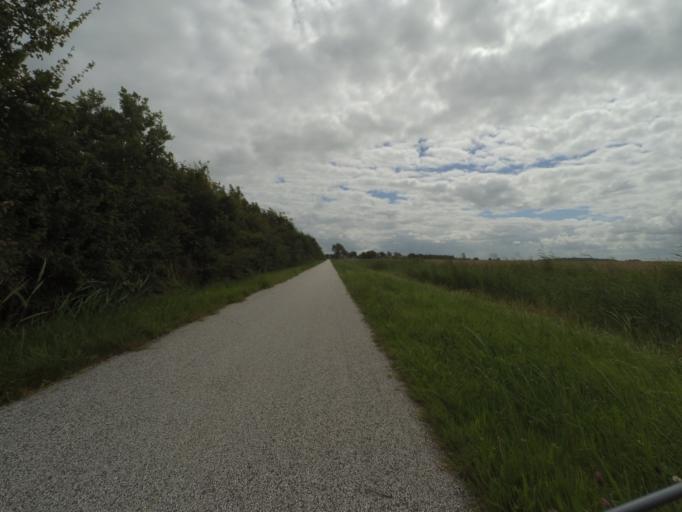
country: NL
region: Friesland
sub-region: Gemeente Kollumerland en Nieuwkruisland
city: Kollum
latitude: 53.3226
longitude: 6.1539
